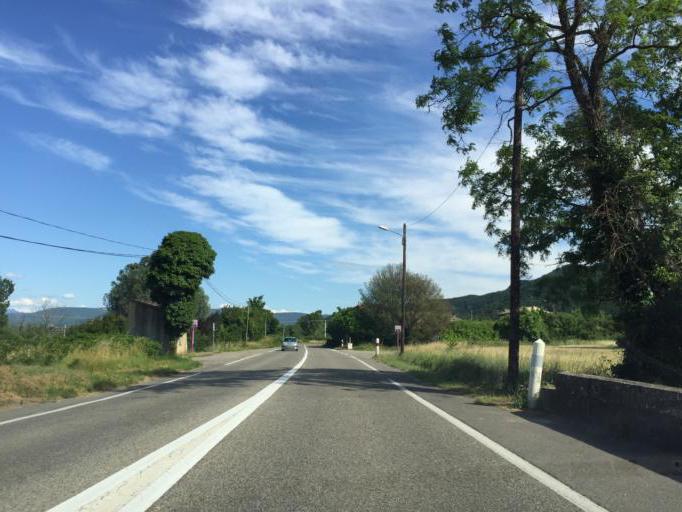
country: FR
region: Rhone-Alpes
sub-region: Departement de l'Ardeche
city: Le Pouzin
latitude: 44.7259
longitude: 4.7425
